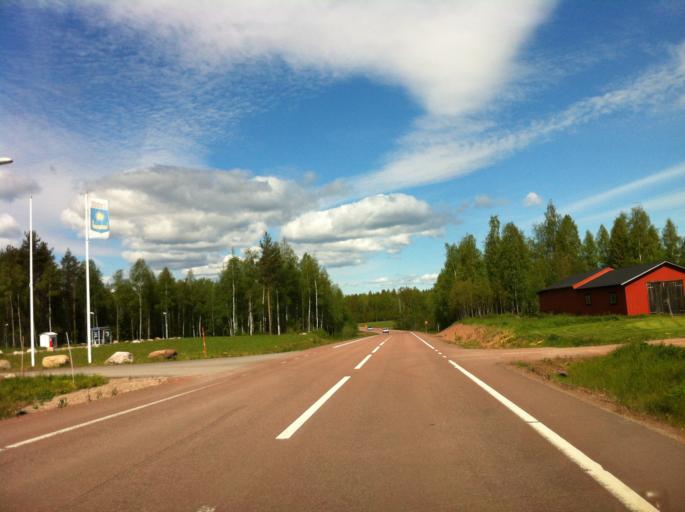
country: SE
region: Dalarna
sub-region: Mora Kommun
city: Mora
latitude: 60.9175
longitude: 14.5990
